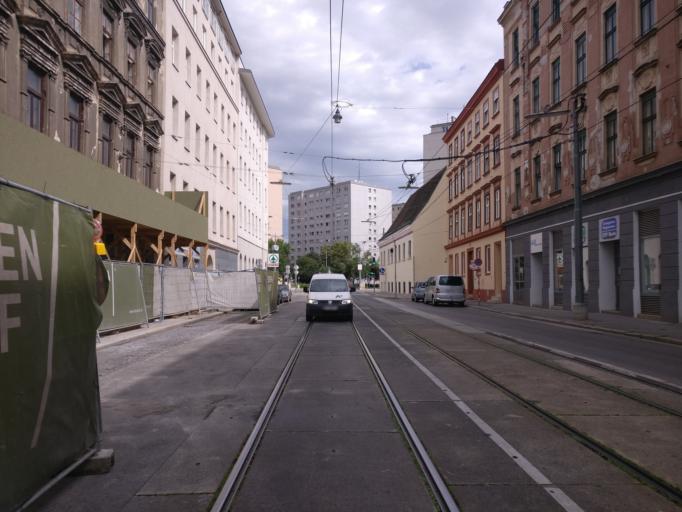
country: AT
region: Vienna
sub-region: Wien Stadt
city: Vienna
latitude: 48.2244
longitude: 16.3832
